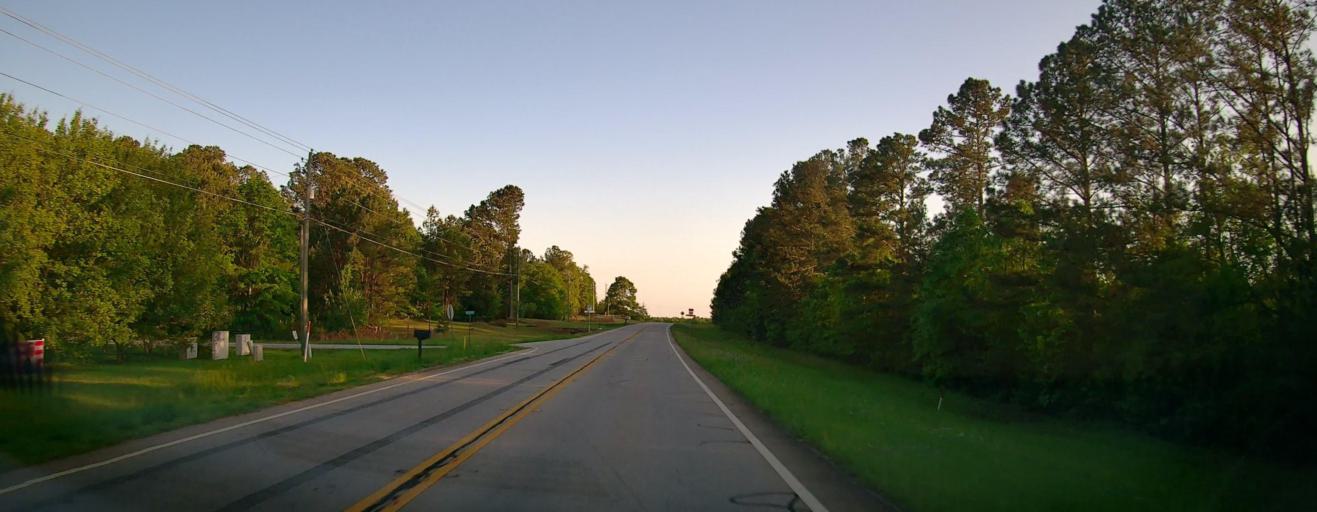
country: US
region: Georgia
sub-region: Newton County
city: Oakwood
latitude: 33.5119
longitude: -83.9479
